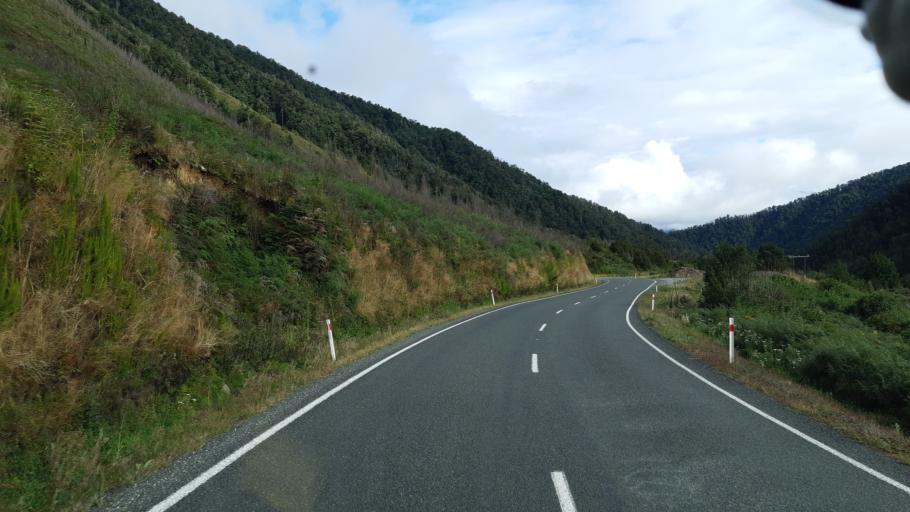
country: NZ
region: West Coast
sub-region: Buller District
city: Westport
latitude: -42.0042
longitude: 172.2305
